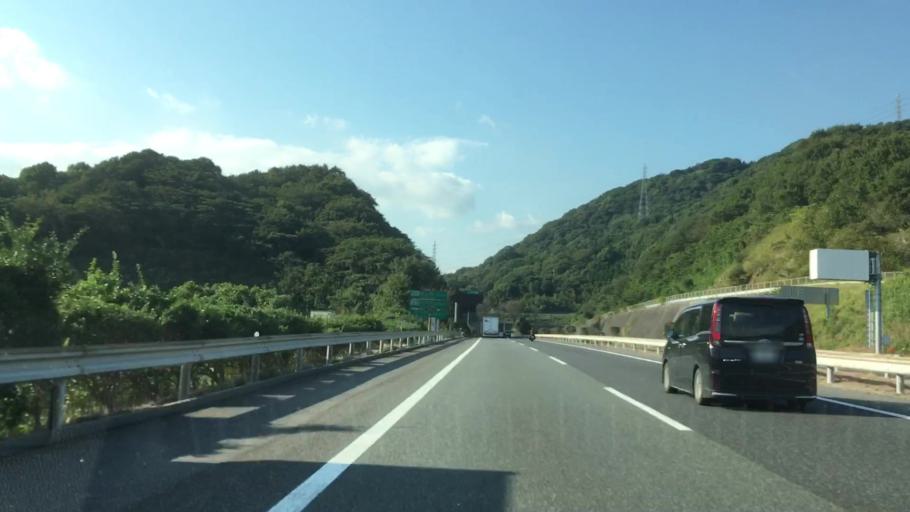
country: JP
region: Yamaguchi
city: Tokuyama
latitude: 34.0576
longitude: 131.8383
